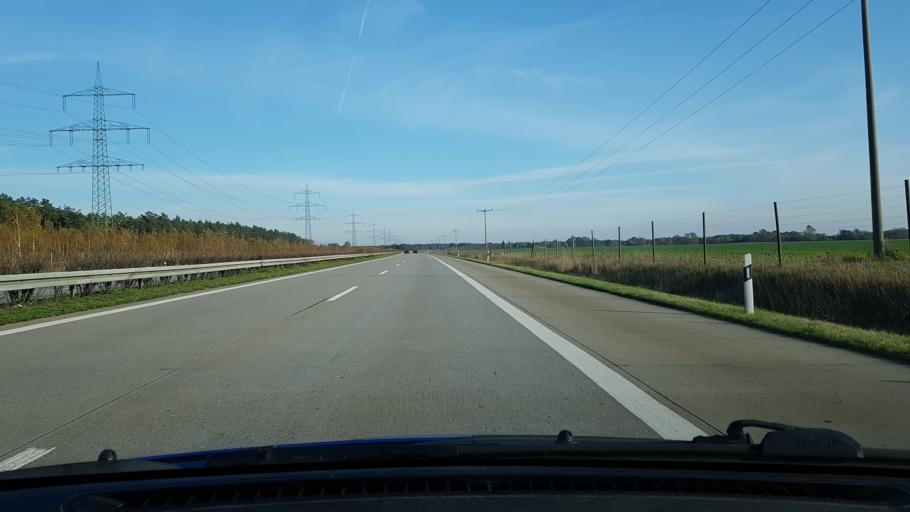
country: DE
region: Mecklenburg-Vorpommern
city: Zarrentin
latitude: 53.5112
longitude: 10.9133
